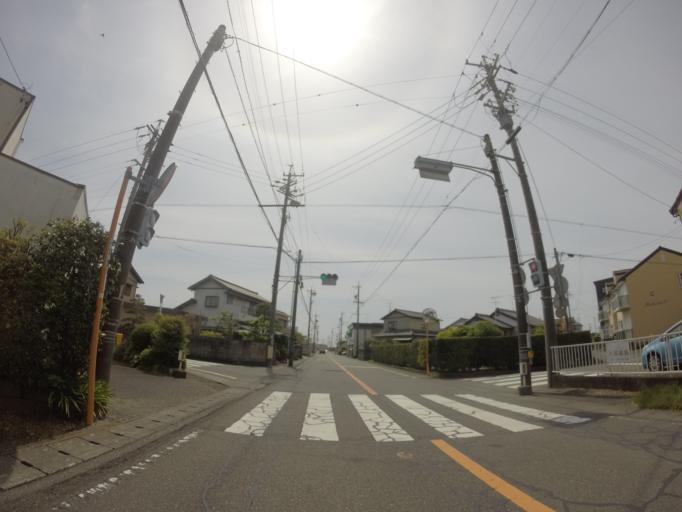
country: JP
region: Shizuoka
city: Fujieda
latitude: 34.8092
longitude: 138.2860
